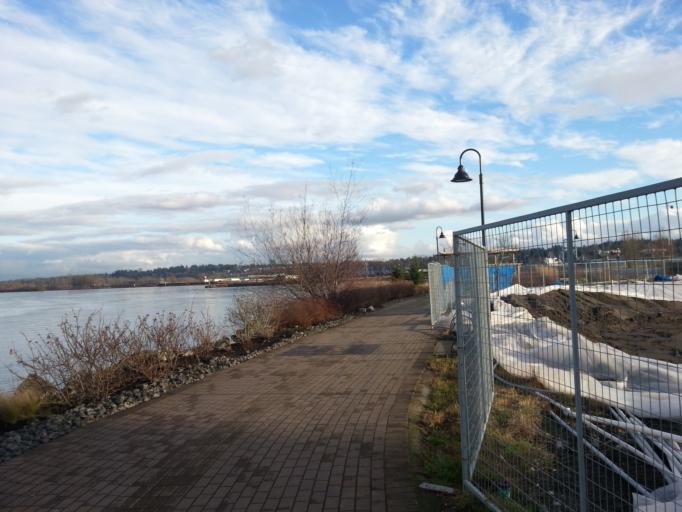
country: CA
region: British Columbia
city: New Westminster
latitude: 49.1958
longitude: -122.9219
